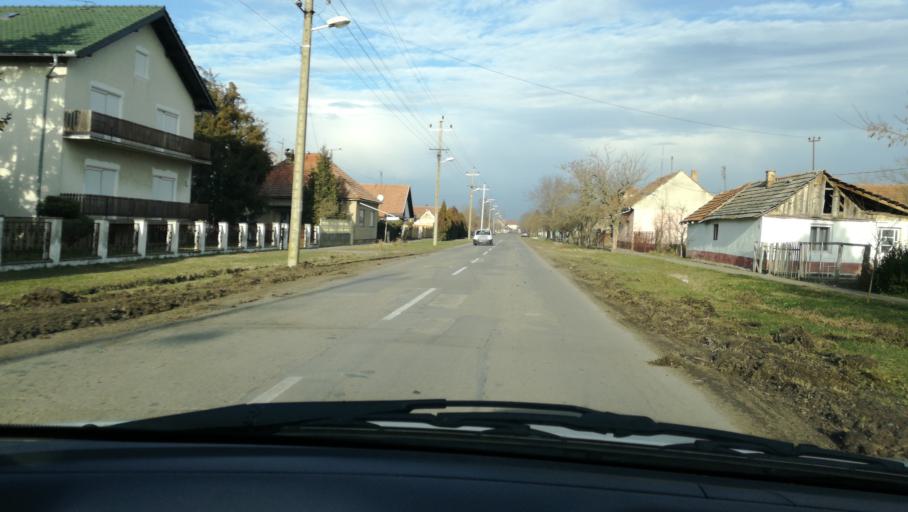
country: RS
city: Rusko Selo
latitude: 45.7643
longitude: 20.5863
